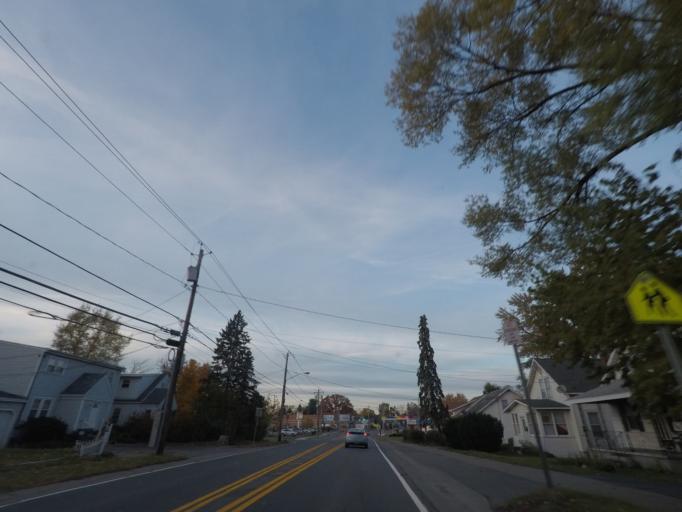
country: US
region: New York
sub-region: Schenectady County
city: Rotterdam
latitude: 42.7855
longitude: -73.9710
